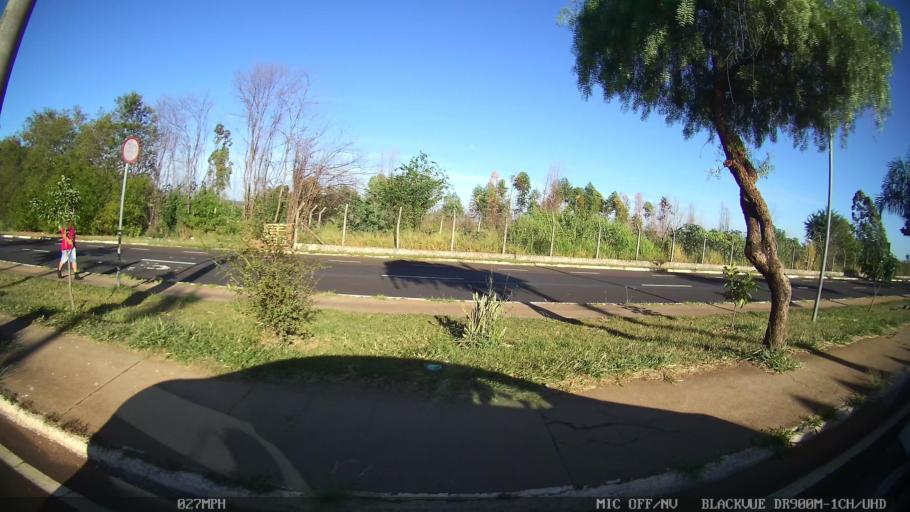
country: BR
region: Sao Paulo
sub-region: Franca
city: Franca
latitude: -20.5792
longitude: -47.3857
